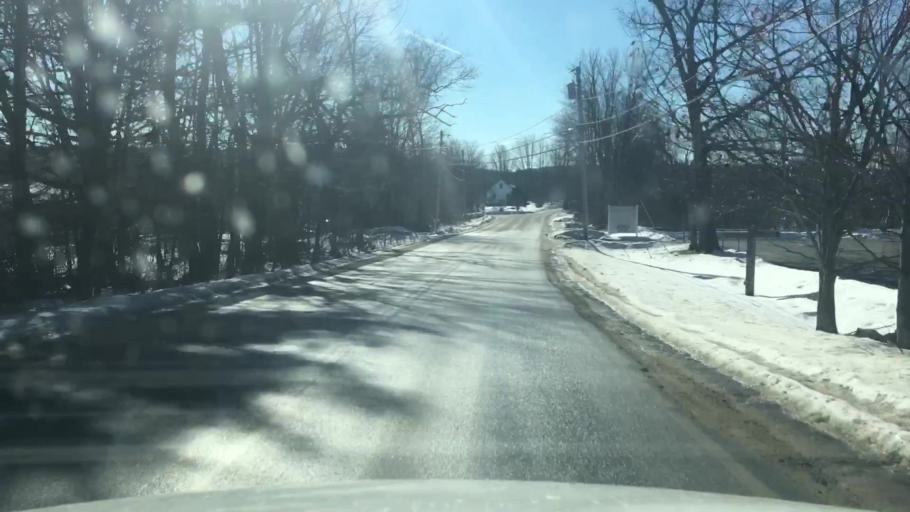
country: US
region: Maine
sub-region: Cumberland County
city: New Gloucester
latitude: 43.8715
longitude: -70.3335
